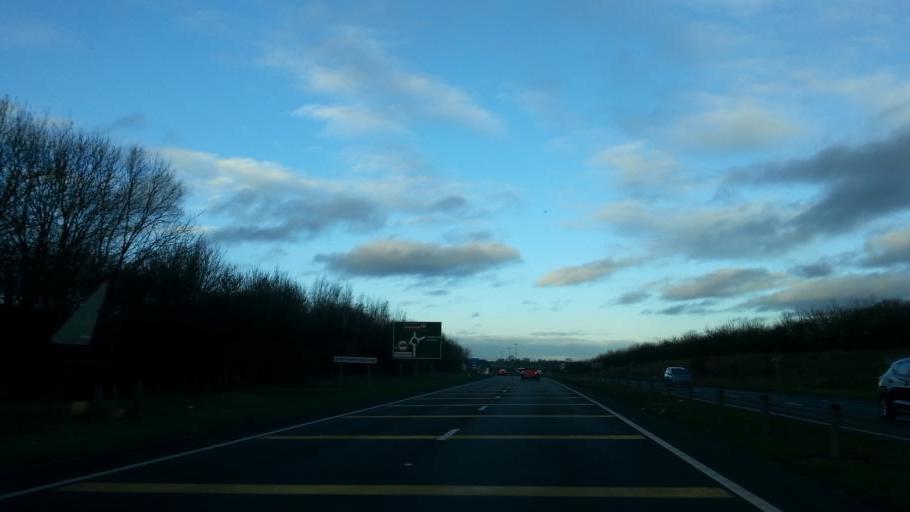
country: GB
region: England
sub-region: Northamptonshire
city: Brackley
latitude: 51.9932
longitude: -1.1638
